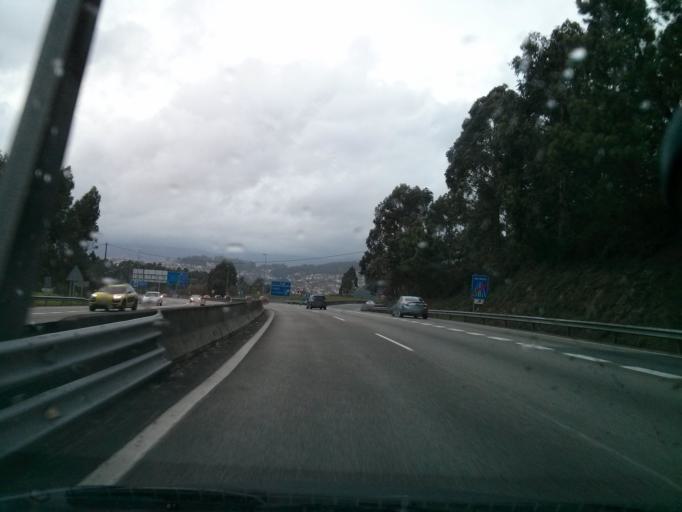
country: ES
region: Galicia
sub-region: Provincia de Pontevedra
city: Porrino
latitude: 42.2087
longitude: -8.6594
